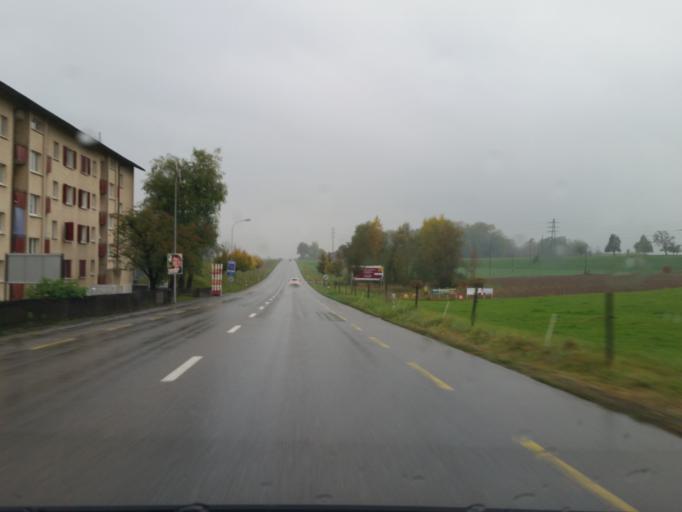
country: CH
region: Thurgau
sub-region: Weinfelden District
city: Sulgen
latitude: 47.5454
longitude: 9.1794
